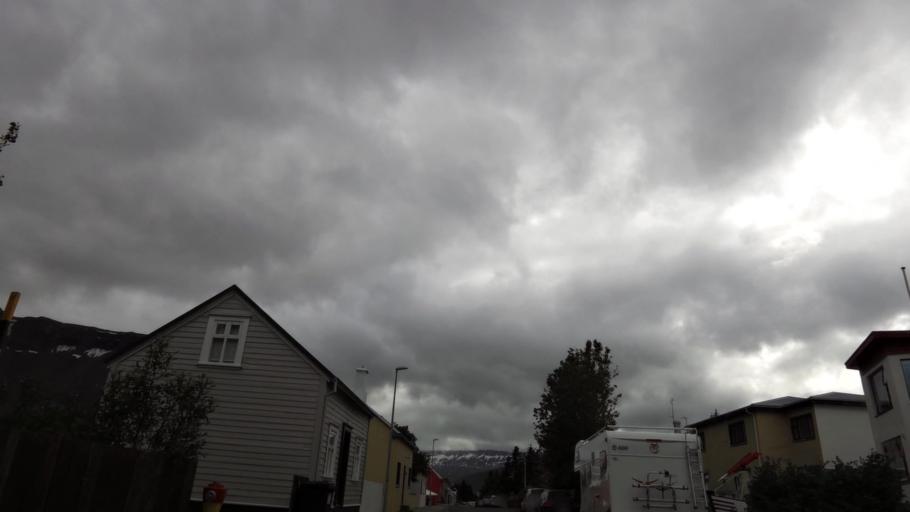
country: IS
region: Westfjords
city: Isafjoerdur
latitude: 66.0786
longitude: -23.1266
